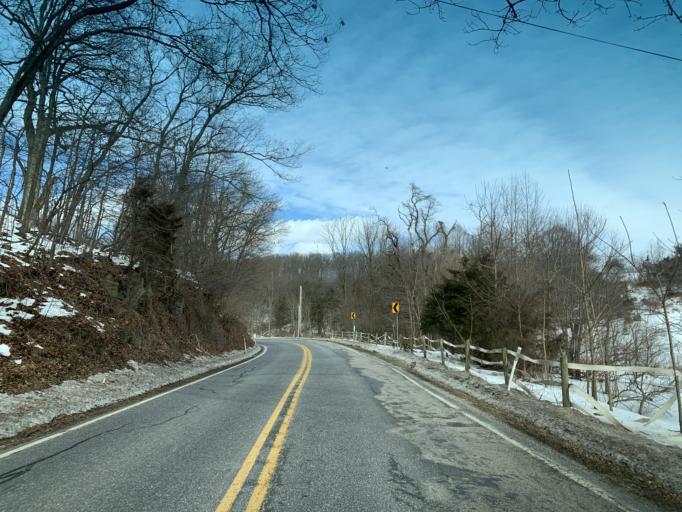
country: US
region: Pennsylvania
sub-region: York County
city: Shrewsbury
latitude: 39.8087
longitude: -76.6290
